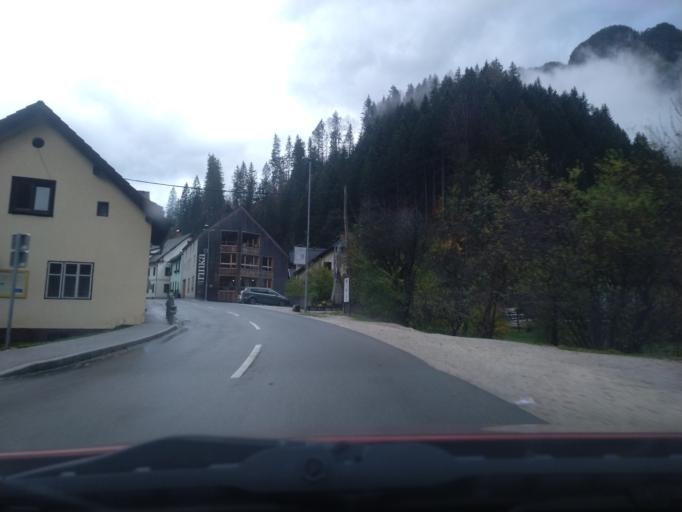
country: SI
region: Solcava
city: Solcava
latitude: 46.4200
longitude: 14.6927
